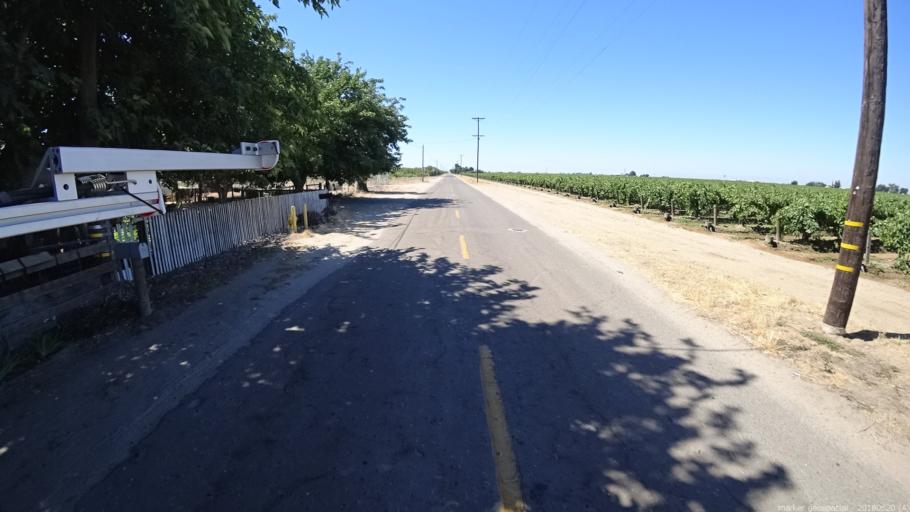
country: US
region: California
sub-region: Fresno County
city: Biola
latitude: 36.8646
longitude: -120.0104
